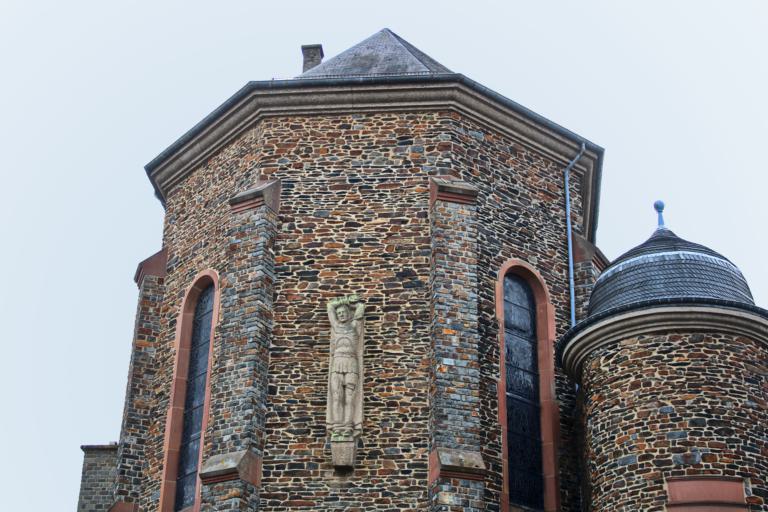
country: LU
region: Diekirch
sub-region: Canton de Wiltz
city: Wiltz
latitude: 49.9659
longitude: 5.9362
